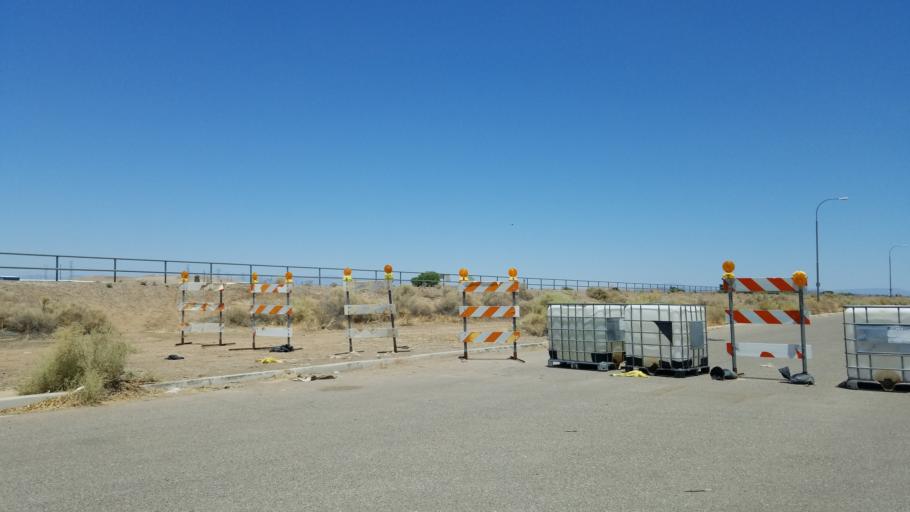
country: US
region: Arizona
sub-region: Maricopa County
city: Litchfield Park
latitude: 33.5170
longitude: -112.2955
